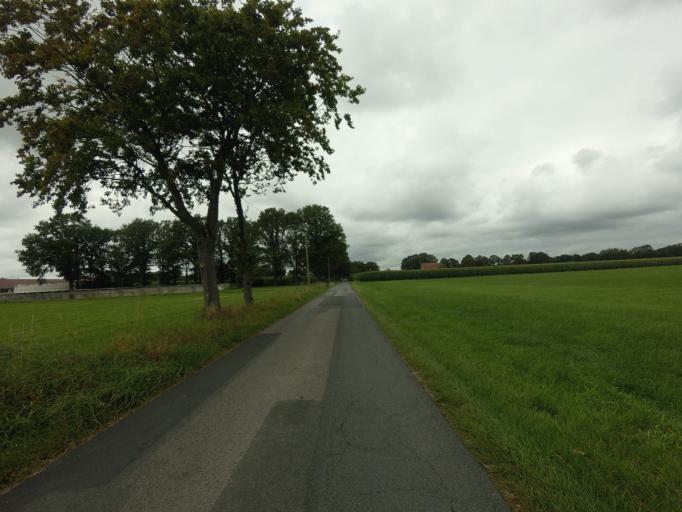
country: NL
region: Overijssel
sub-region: Gemeente Losser
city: Losser
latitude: 52.2576
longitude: 7.0707
